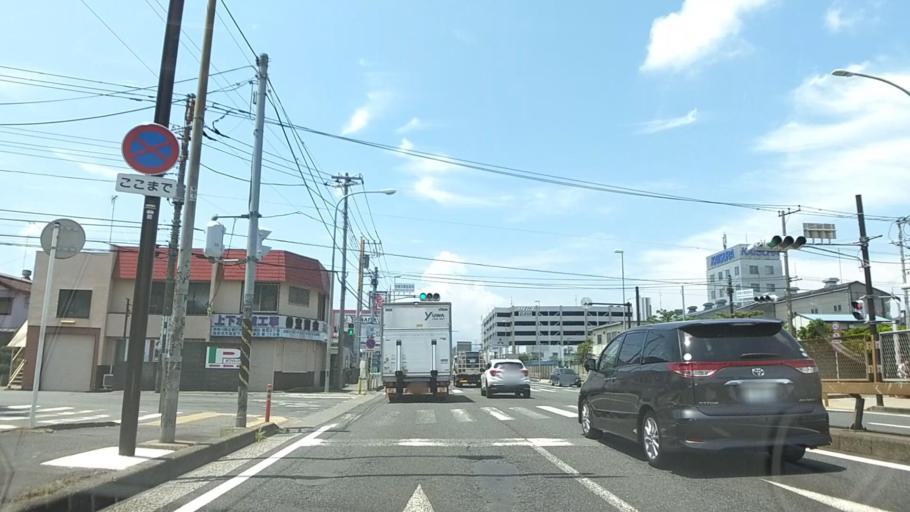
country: JP
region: Kanagawa
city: Minami-rinkan
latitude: 35.4786
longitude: 139.4346
